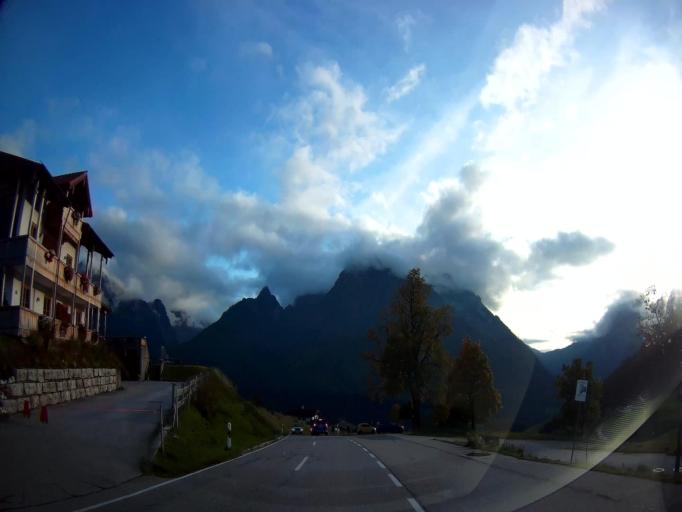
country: DE
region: Bavaria
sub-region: Upper Bavaria
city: Ramsau
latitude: 47.6219
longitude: 12.9035
